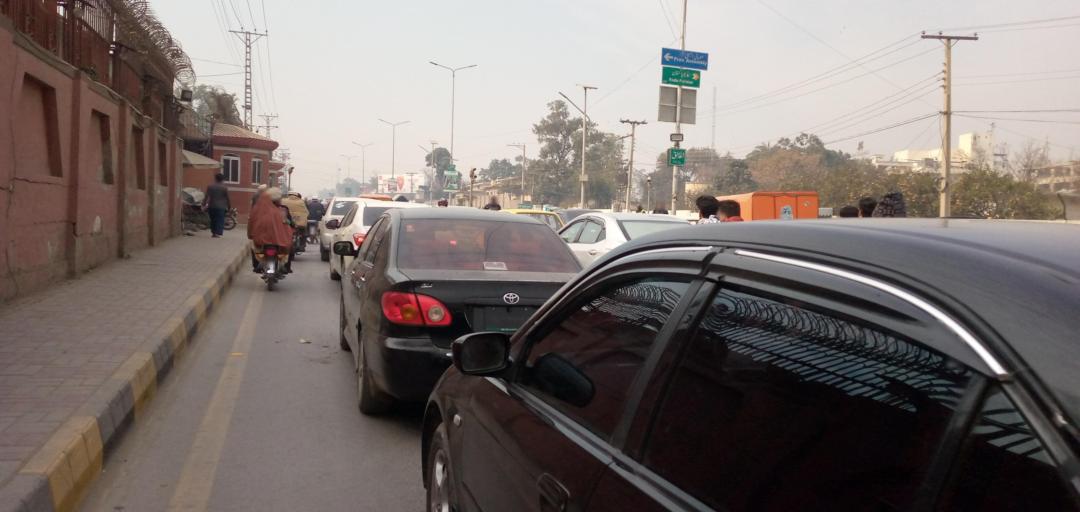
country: PK
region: Khyber Pakhtunkhwa
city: Peshawar
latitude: 34.0144
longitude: 71.5662
